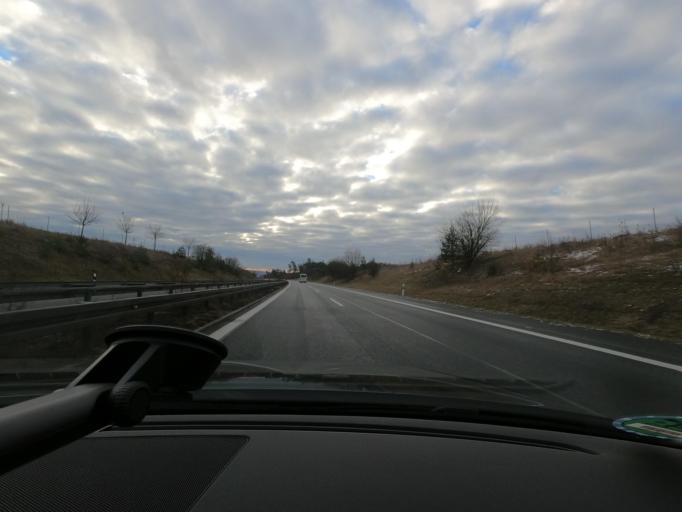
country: DE
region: Bavaria
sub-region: Upper Franconia
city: Meeder
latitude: 50.3290
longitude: 10.9401
